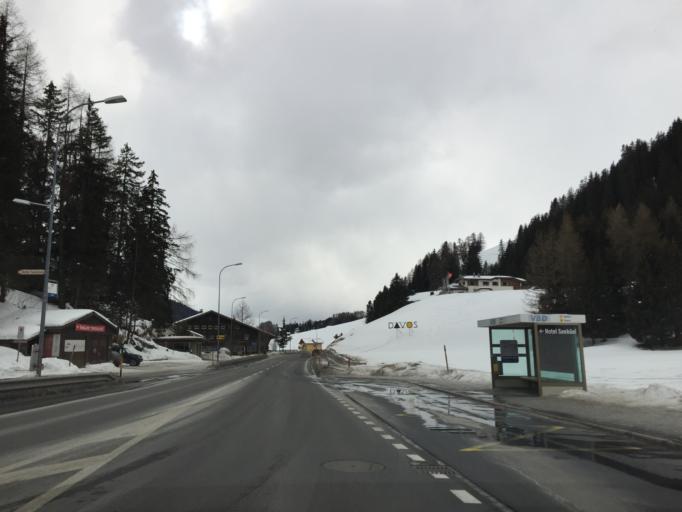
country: CH
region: Grisons
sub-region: Praettigau/Davos District
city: Davos
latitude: 46.8248
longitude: 9.8534
